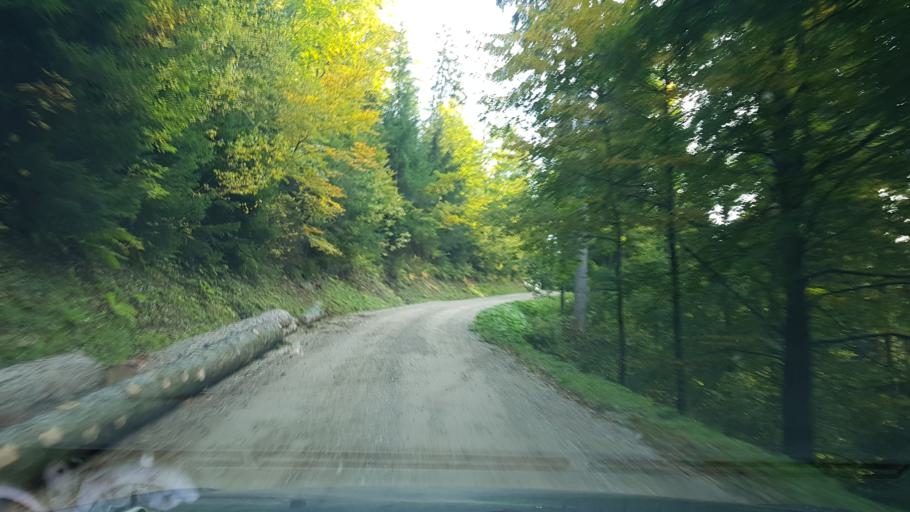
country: SI
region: Slovenj Gradec
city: Legen
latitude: 46.5195
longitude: 15.1325
